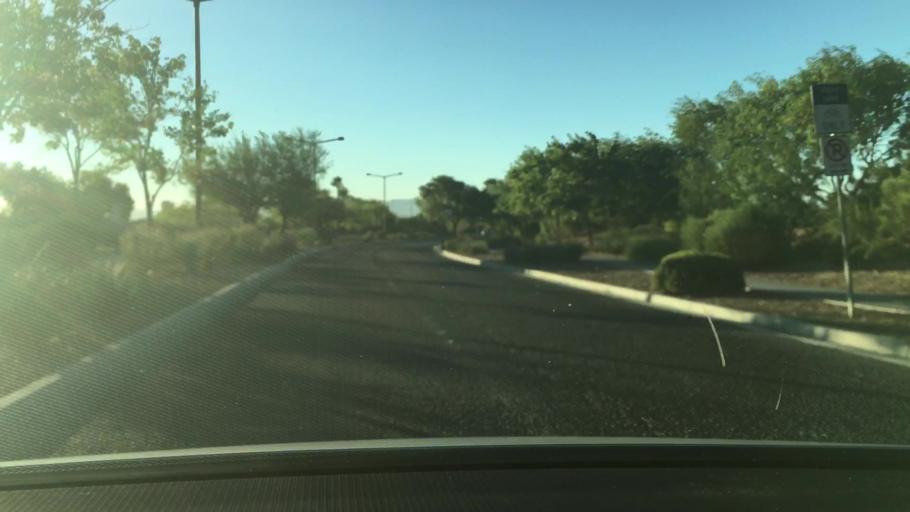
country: US
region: Nevada
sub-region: Clark County
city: Summerlin South
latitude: 36.1247
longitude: -115.3378
